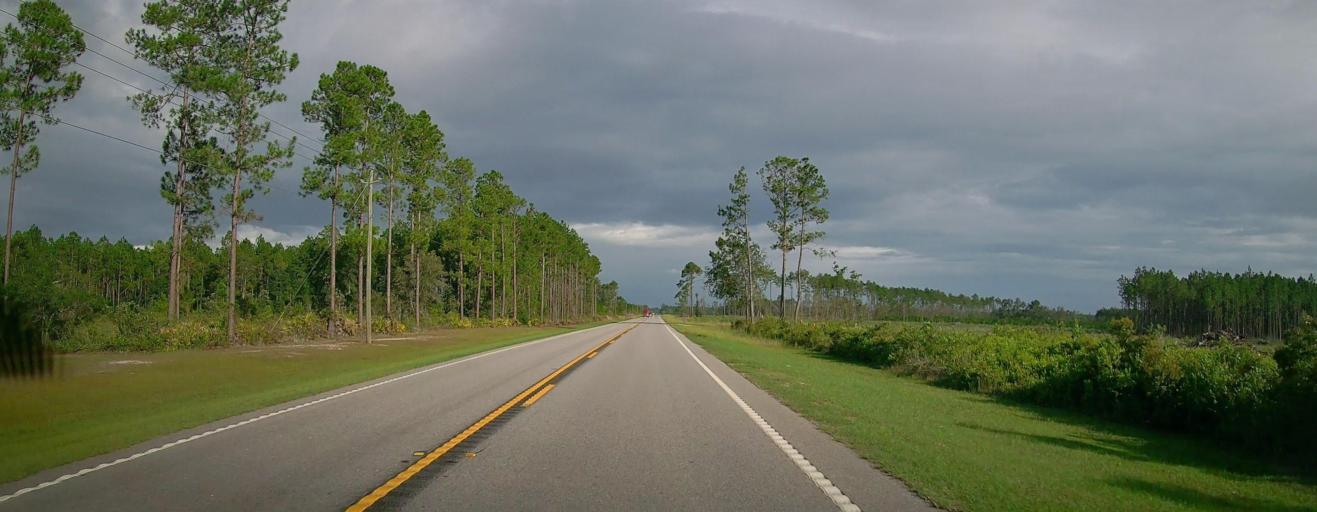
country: US
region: Georgia
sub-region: Coffee County
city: Nicholls
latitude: 31.3795
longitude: -82.6422
